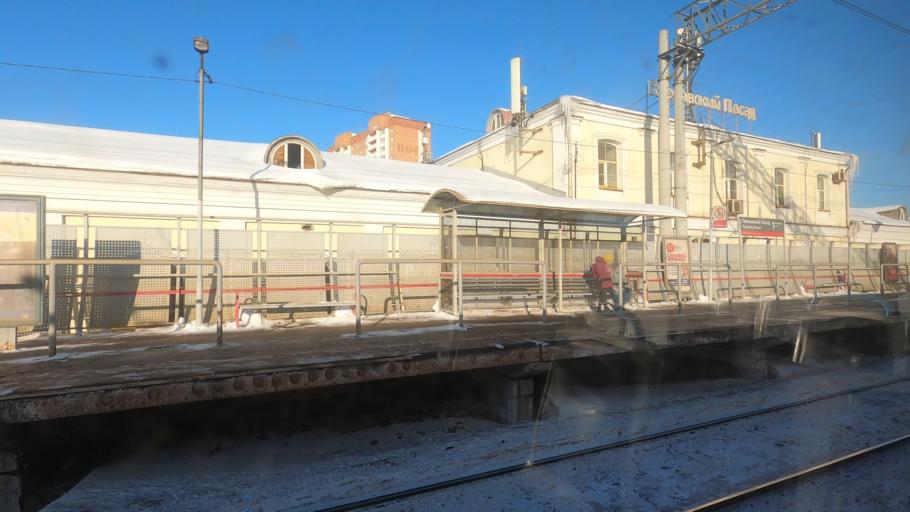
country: RU
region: Moskovskaya
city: Pavlovskiy Posad
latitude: 55.7758
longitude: 38.6745
